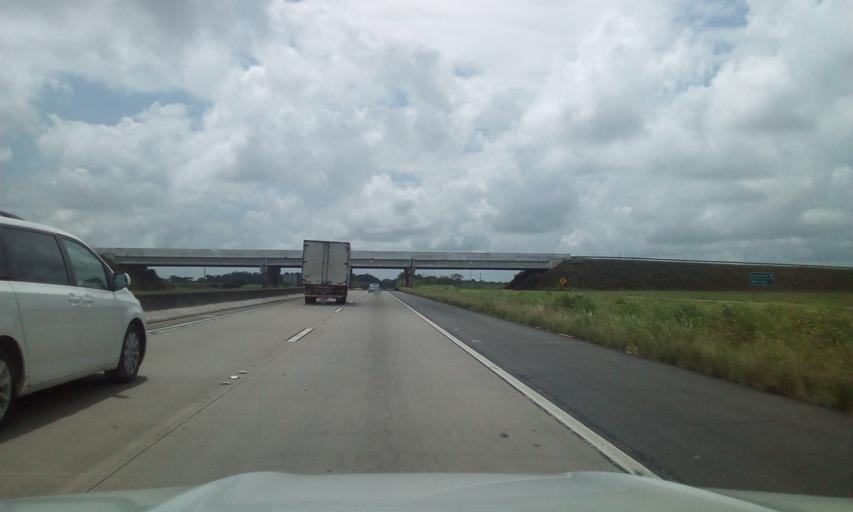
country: BR
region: Pernambuco
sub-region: Goiana
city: Goiana
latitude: -7.6142
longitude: -34.9732
